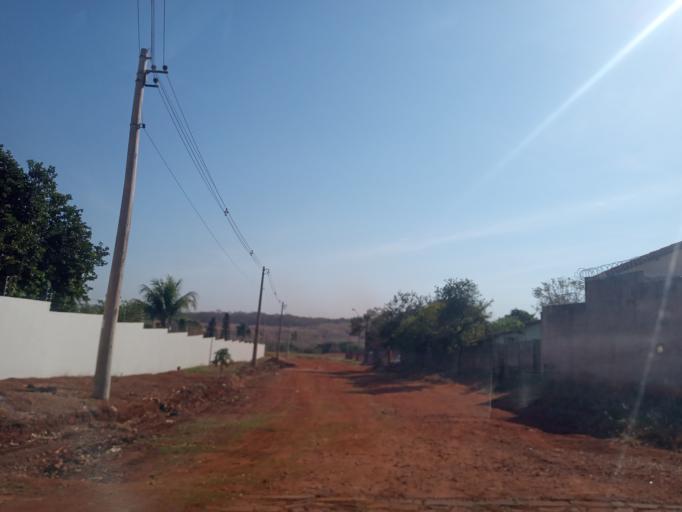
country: BR
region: Minas Gerais
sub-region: Ituiutaba
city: Ituiutaba
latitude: -18.9515
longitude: -49.4634
